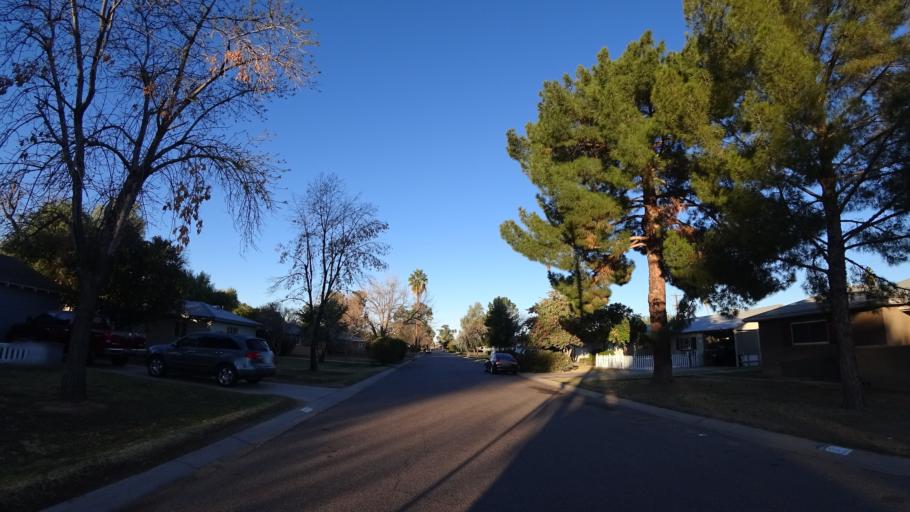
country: US
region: Arizona
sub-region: Maricopa County
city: Paradise Valley
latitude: 33.4831
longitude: -111.9914
